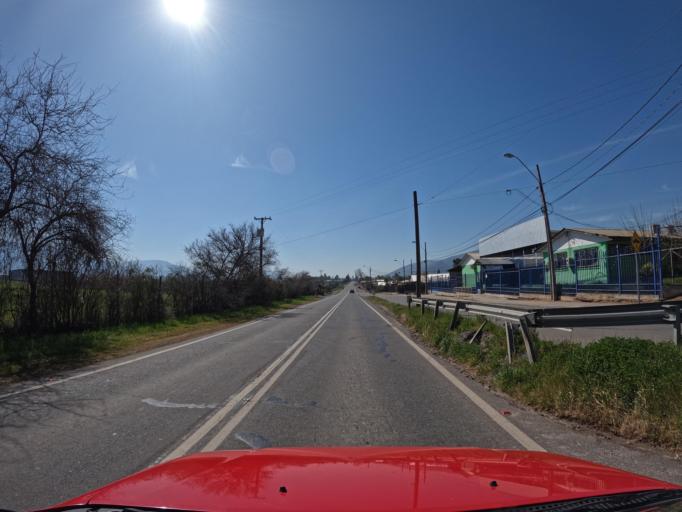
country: CL
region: Maule
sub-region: Provincia de Curico
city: Rauco
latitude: -35.0427
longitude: -71.4584
